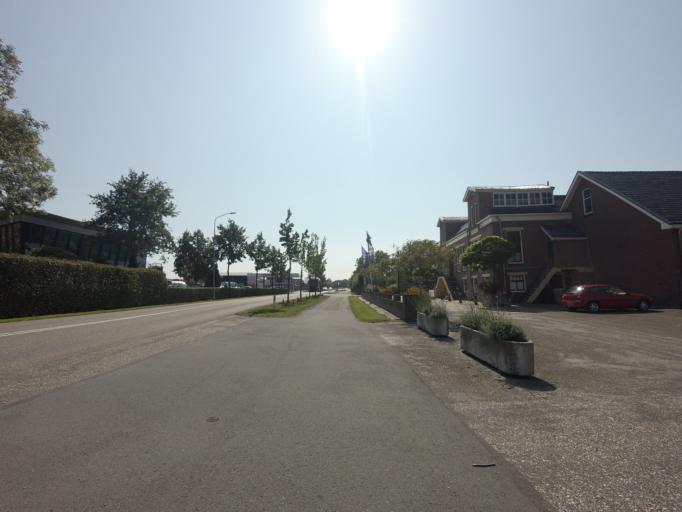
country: NL
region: Groningen
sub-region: Gemeente Zuidhorn
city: Grijpskerk
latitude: 53.2680
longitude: 6.3070
